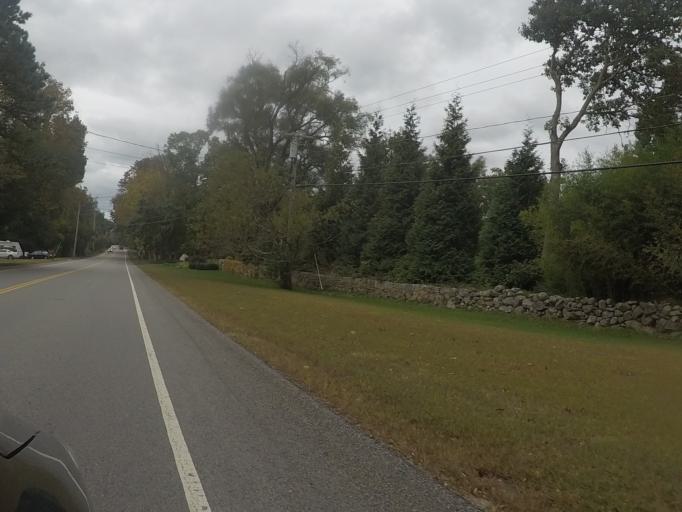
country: US
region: Massachusetts
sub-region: Bristol County
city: Smith Mills
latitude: 41.5963
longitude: -71.0025
